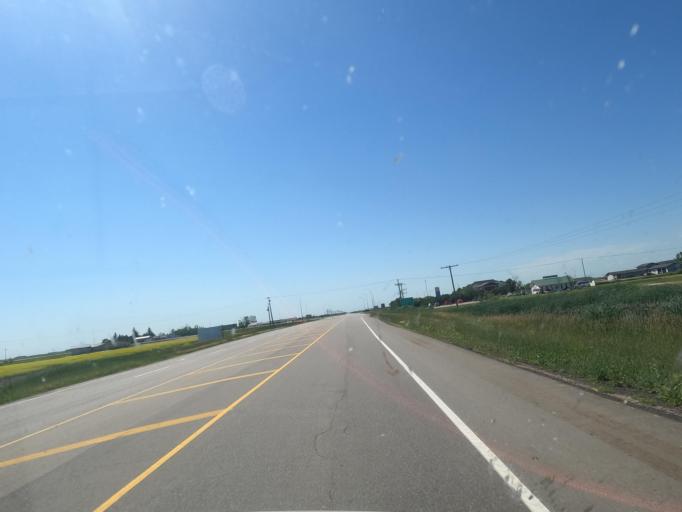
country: CA
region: Saskatchewan
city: Estevan
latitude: 49.6683
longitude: -103.0181
